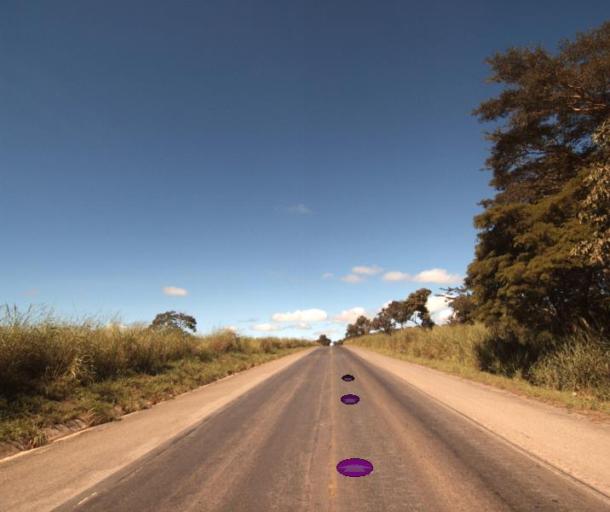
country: BR
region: Goias
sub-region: Itapaci
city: Itapaci
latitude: -15.0629
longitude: -49.4525
